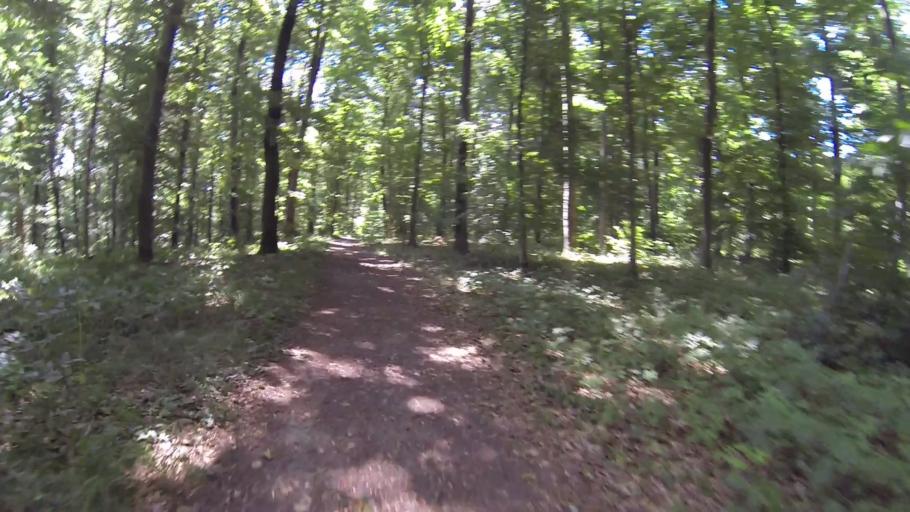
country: DE
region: Baden-Wuerttemberg
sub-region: Regierungsbezirk Stuttgart
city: Herbrechtingen
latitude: 48.6087
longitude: 10.1742
